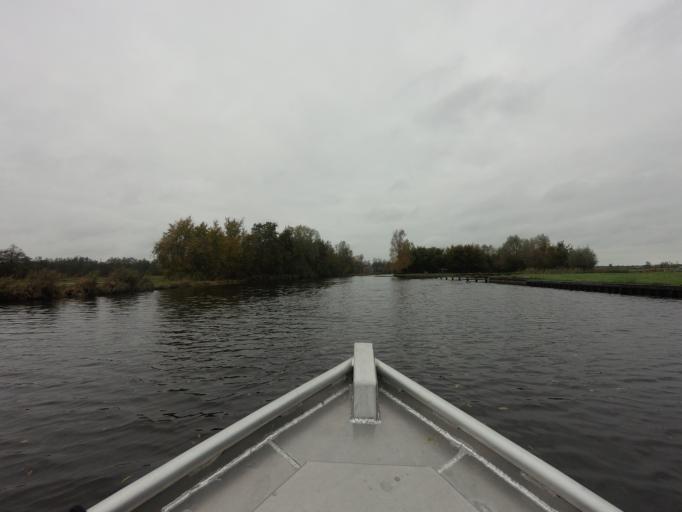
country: NL
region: Overijssel
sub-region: Gemeente Steenwijkerland
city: Oldemarkt
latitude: 52.7732
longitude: 5.9845
